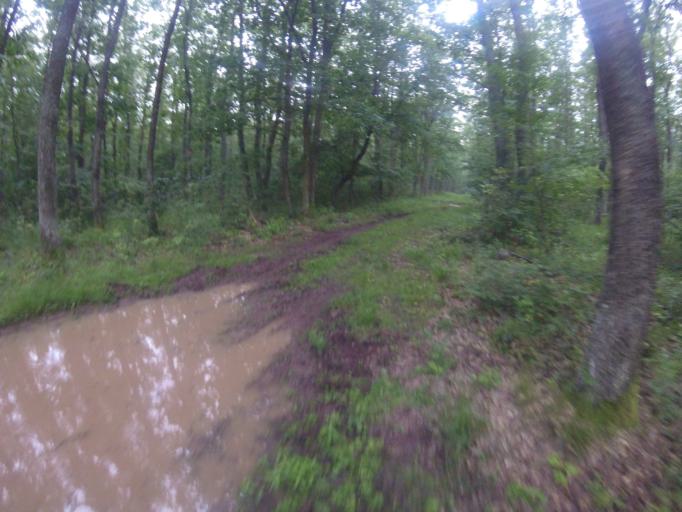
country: HU
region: Veszprem
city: Urkut
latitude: 47.0262
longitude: 17.6656
